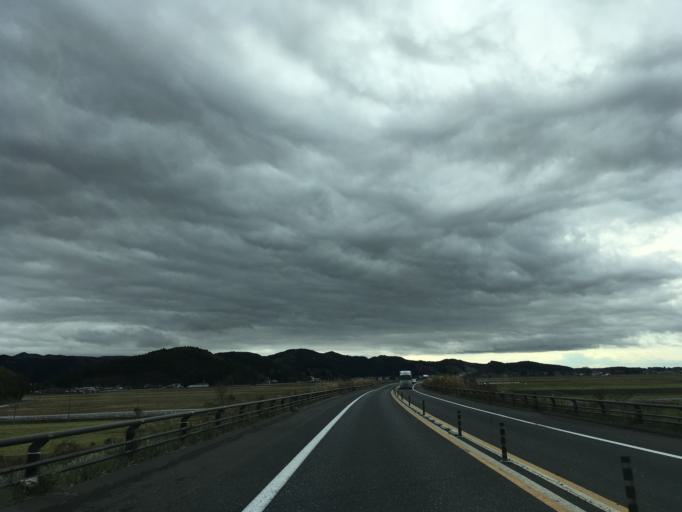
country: JP
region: Miyagi
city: Wakuya
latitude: 38.6226
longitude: 141.2855
